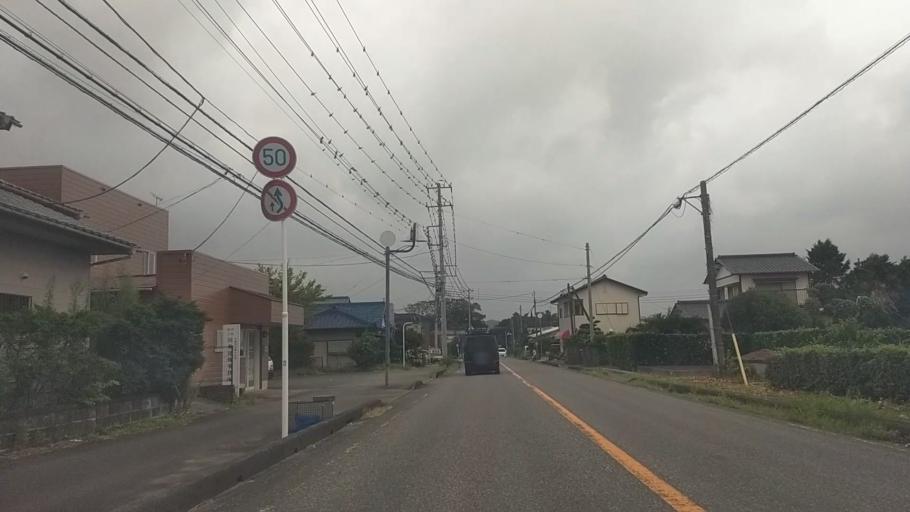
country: JP
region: Chiba
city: Kawaguchi
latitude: 35.1316
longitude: 140.0153
